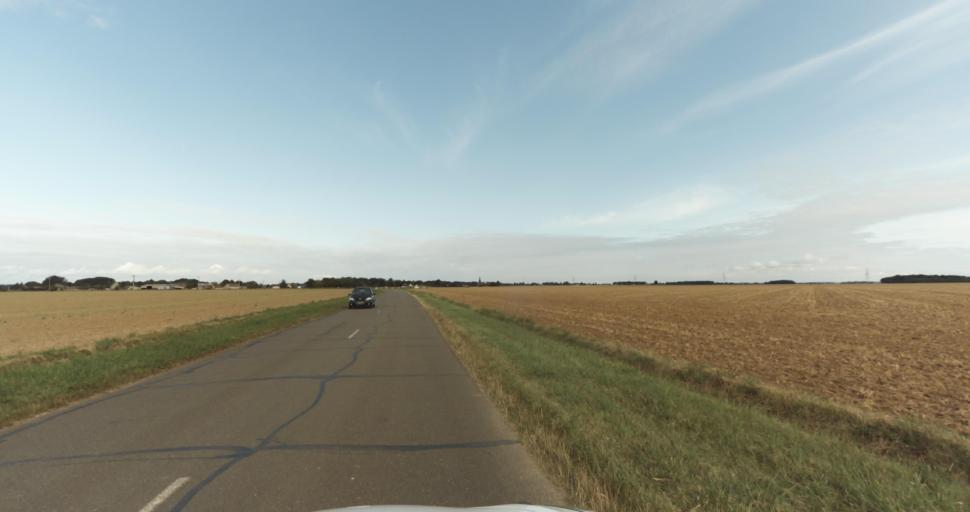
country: FR
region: Haute-Normandie
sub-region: Departement de l'Eure
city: La Madeleine-de-Nonancourt
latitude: 48.8375
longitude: 1.1742
